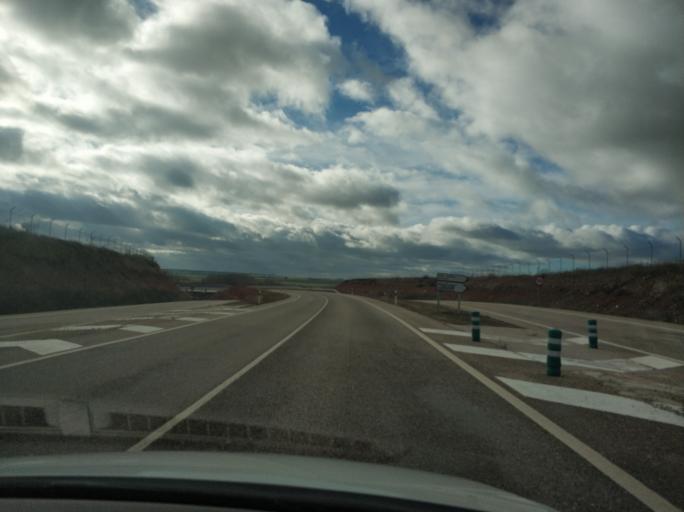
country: ES
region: Castille and Leon
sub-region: Provincia de Segovia
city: Ayllon
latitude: 41.4188
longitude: -3.4043
